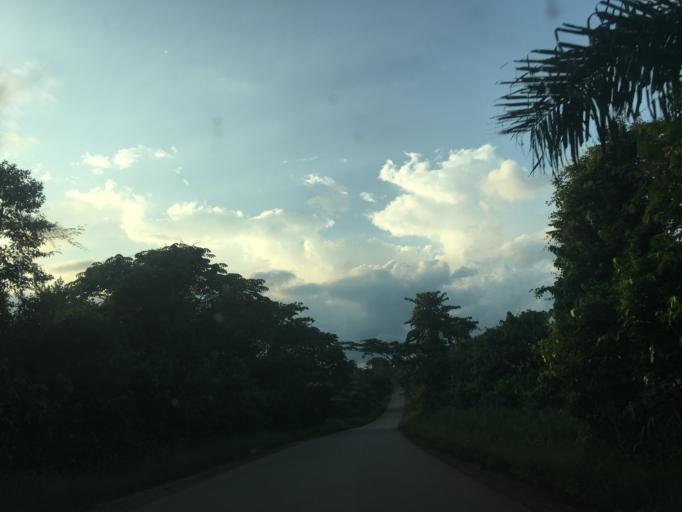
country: GH
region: Western
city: Bibiani
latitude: 6.6697
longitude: -2.4332
